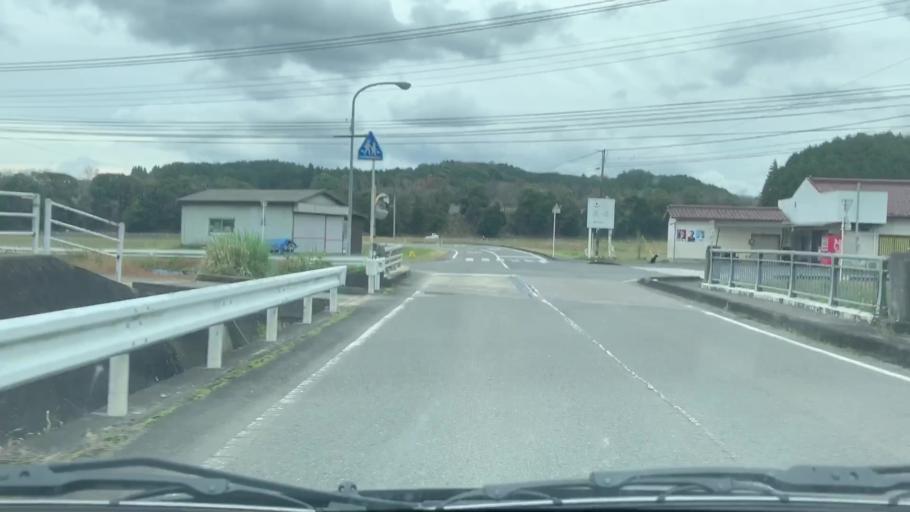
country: JP
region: Saga Prefecture
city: Ureshinomachi-shimojuku
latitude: 33.1277
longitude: 129.9800
